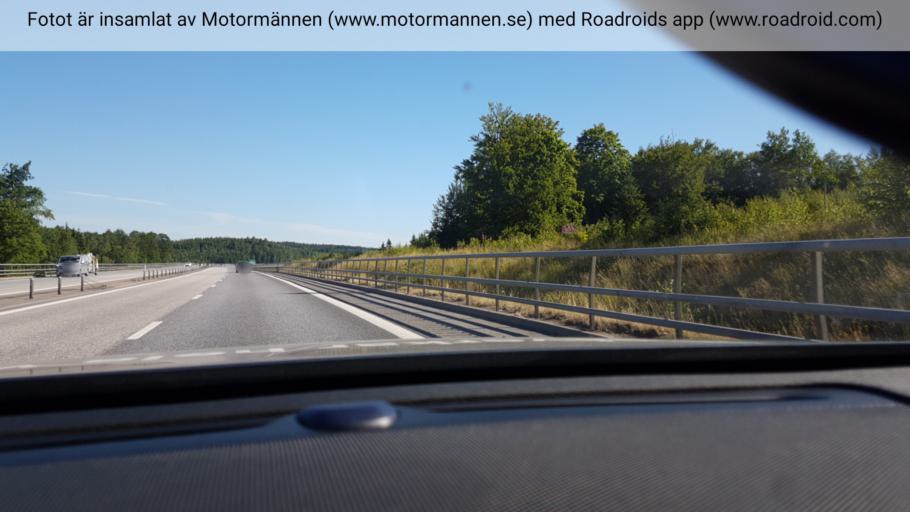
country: SE
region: Kronoberg
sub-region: Markaryds Kommun
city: Markaryd
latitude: 56.4965
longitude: 13.6526
